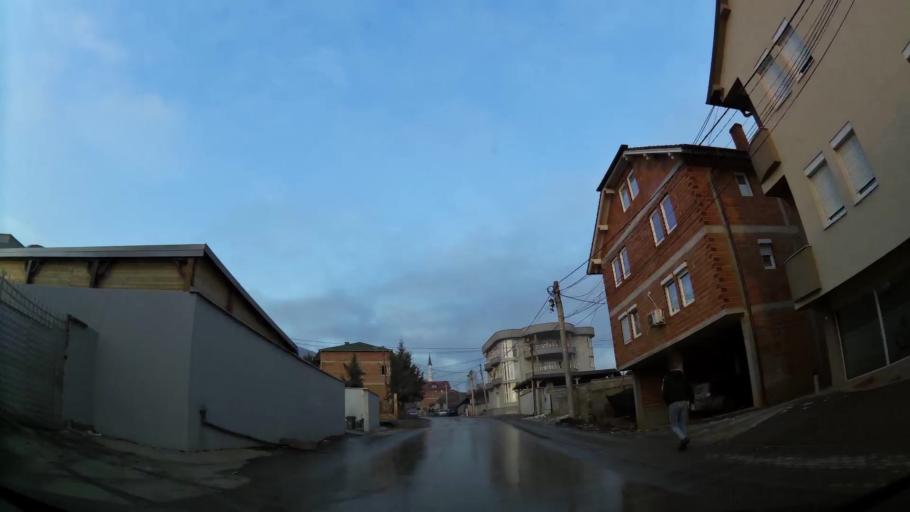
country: MK
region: Aracinovo
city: Arachinovo
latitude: 42.0288
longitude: 21.5647
